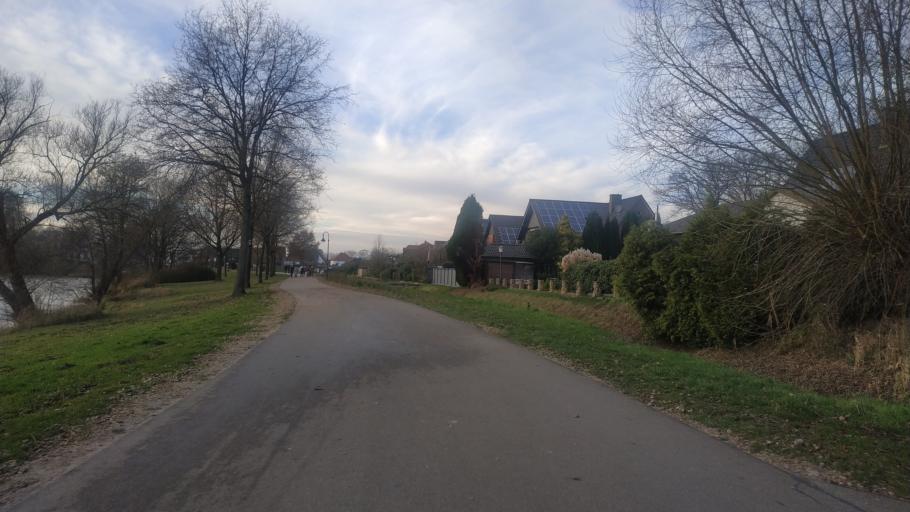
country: DE
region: North Rhine-Westphalia
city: Ibbenburen
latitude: 52.2688
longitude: 7.7259
